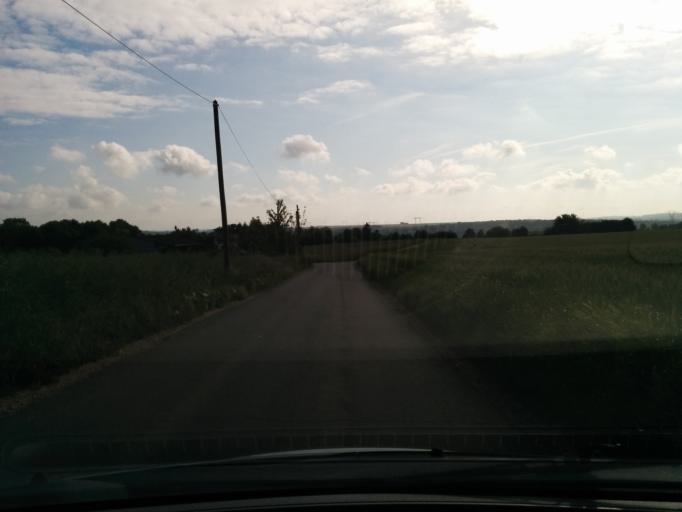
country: FR
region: Ile-de-France
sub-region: Departement des Yvelines
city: Oinville-sur-Montcient
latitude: 49.0243
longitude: 1.8423
